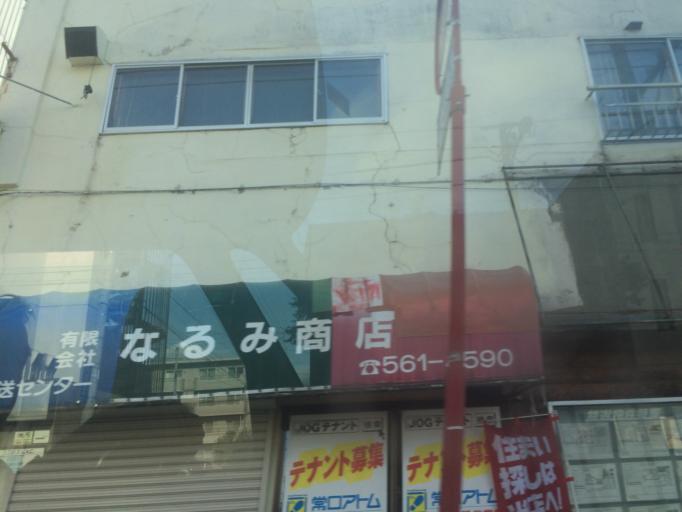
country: JP
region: Hokkaido
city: Sapporo
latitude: 43.0430
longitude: 141.3504
